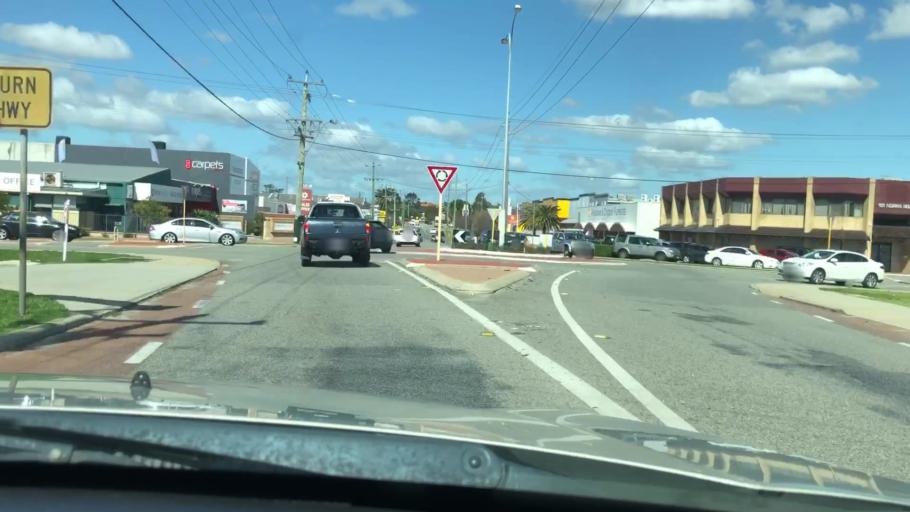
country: AU
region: Western Australia
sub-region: Melville
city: Myaree
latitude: -32.0431
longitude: 115.8223
